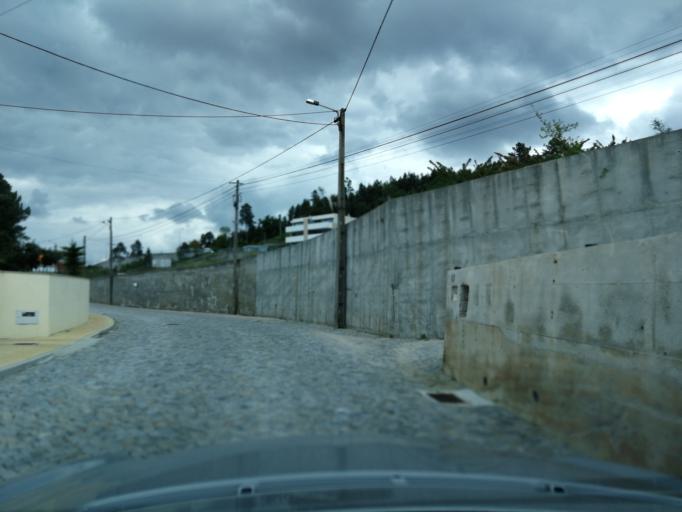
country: PT
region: Braga
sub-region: Braga
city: Braga
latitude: 41.5284
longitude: -8.3953
